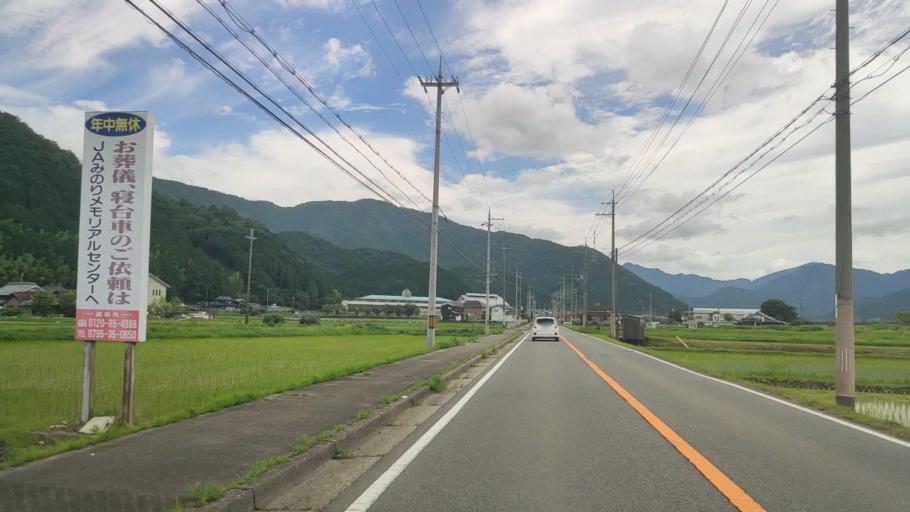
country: JP
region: Hyogo
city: Nishiwaki
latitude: 35.0990
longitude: 134.8977
